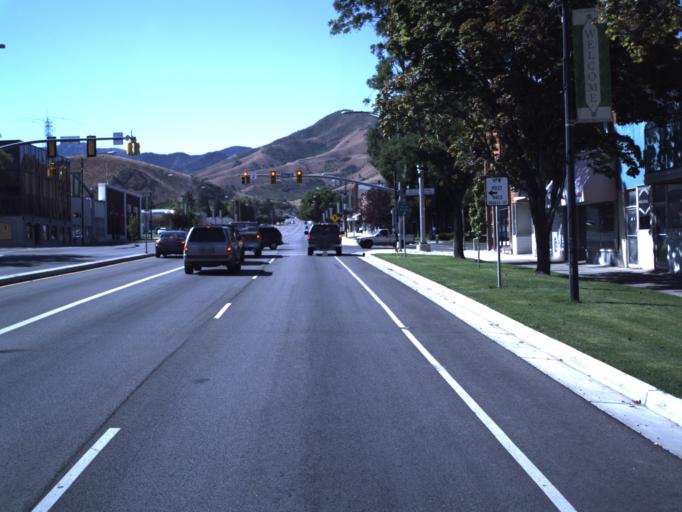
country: US
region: Utah
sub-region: Tooele County
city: Tooele
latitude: 40.5313
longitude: -112.2986
